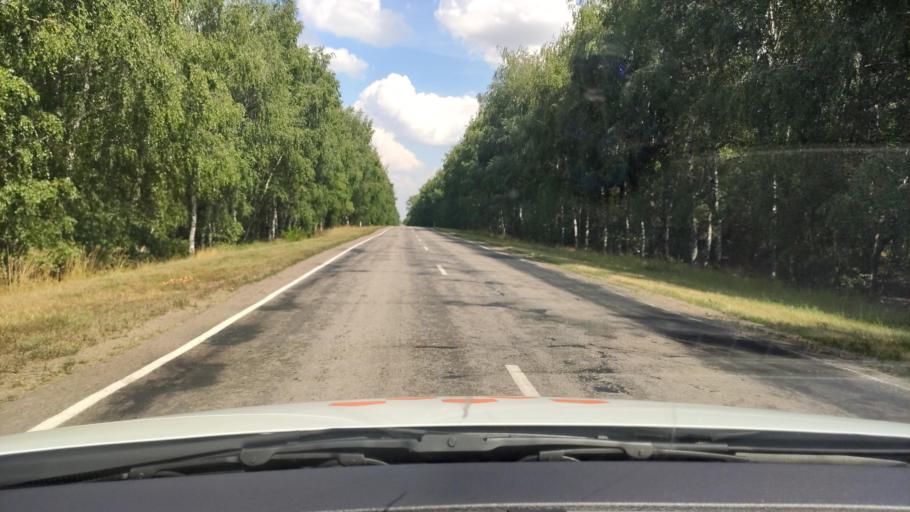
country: RU
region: Voronezj
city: Sadovoye
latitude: 51.7818
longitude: 40.5491
